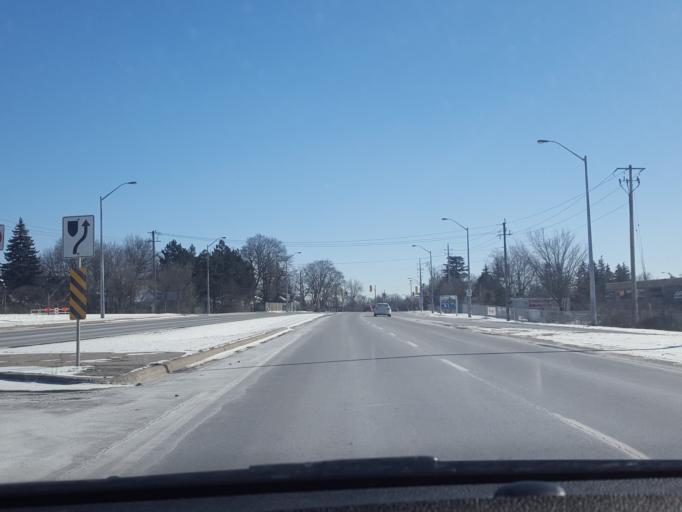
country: CA
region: Ontario
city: Cambridge
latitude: 43.4011
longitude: -80.3778
